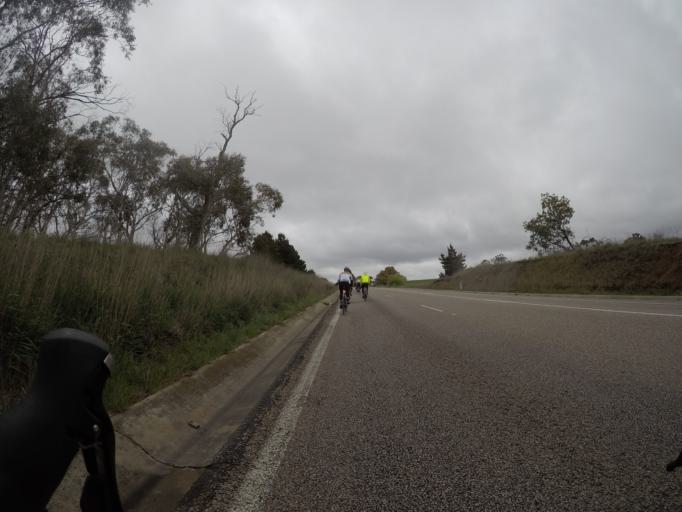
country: AU
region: New South Wales
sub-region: Lithgow
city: Portland
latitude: -33.4340
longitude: 149.9168
